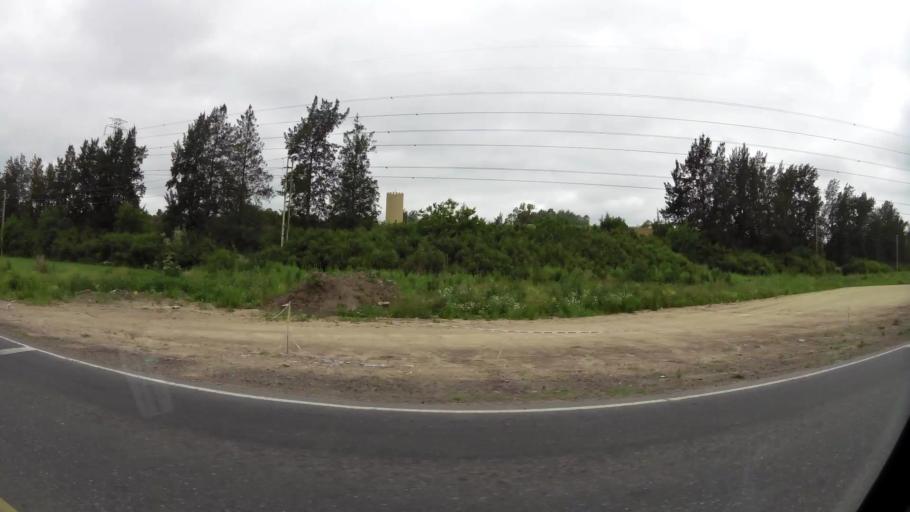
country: AR
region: Buenos Aires
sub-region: Partido de Ezeiza
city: Ezeiza
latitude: -34.9010
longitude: -58.5090
